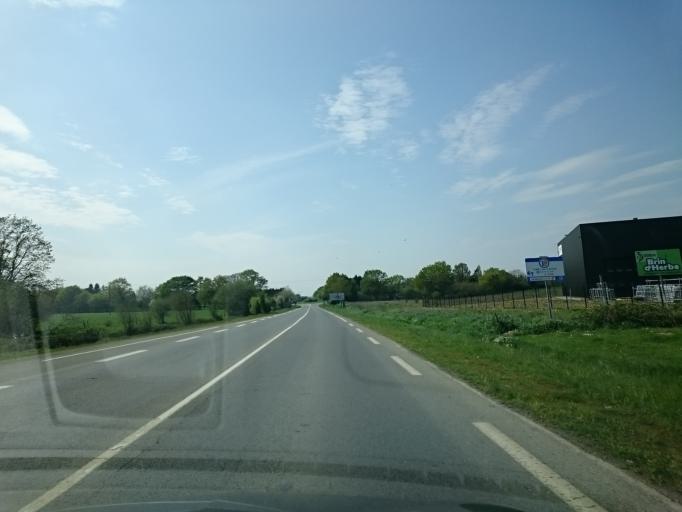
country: FR
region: Brittany
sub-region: Departement d'Ille-et-Vilaine
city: Chantepie
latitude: 48.0793
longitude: -1.5995
